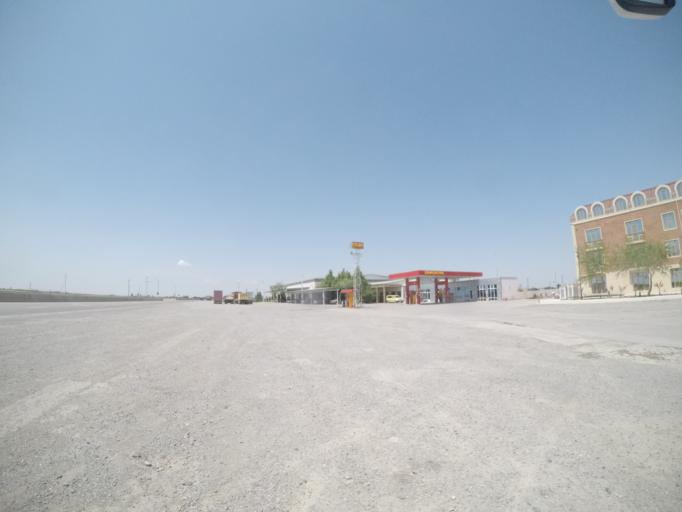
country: AZ
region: Kurdamir Rayon
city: Kyurdarmir
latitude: 40.3157
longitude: 48.1715
